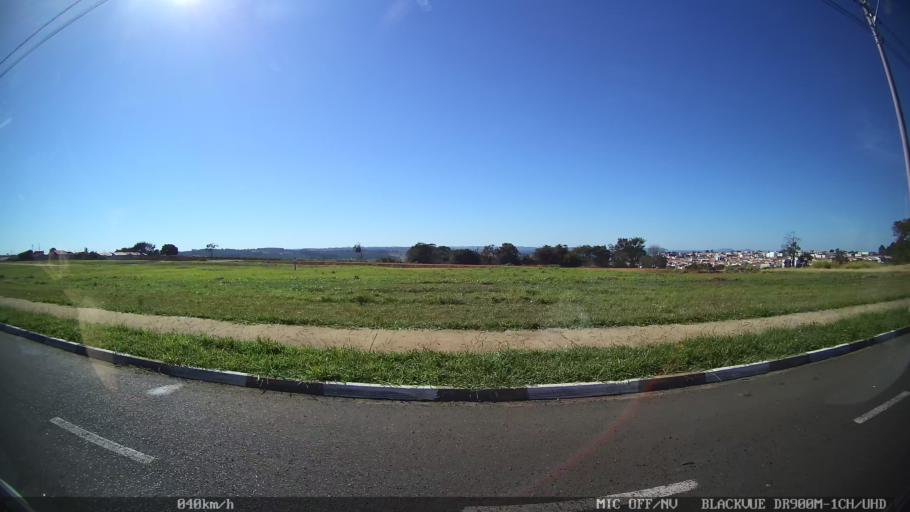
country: BR
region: Sao Paulo
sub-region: Franca
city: Franca
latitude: -20.5610
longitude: -47.3590
